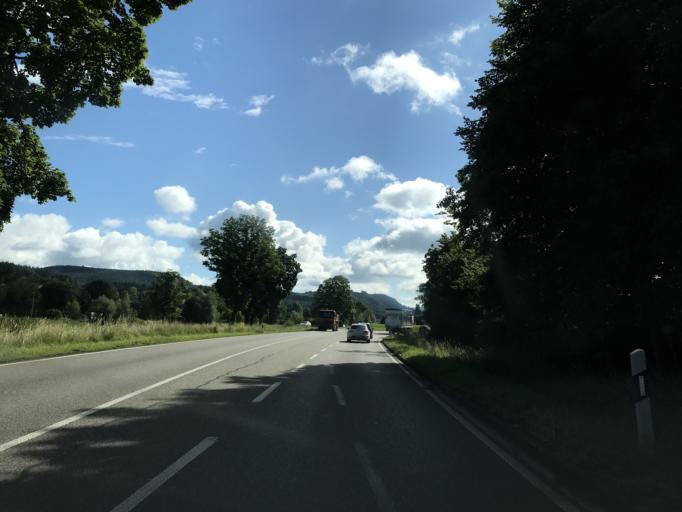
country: DE
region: Baden-Wuerttemberg
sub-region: Freiburg Region
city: Steinen
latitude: 47.6394
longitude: 7.7411
